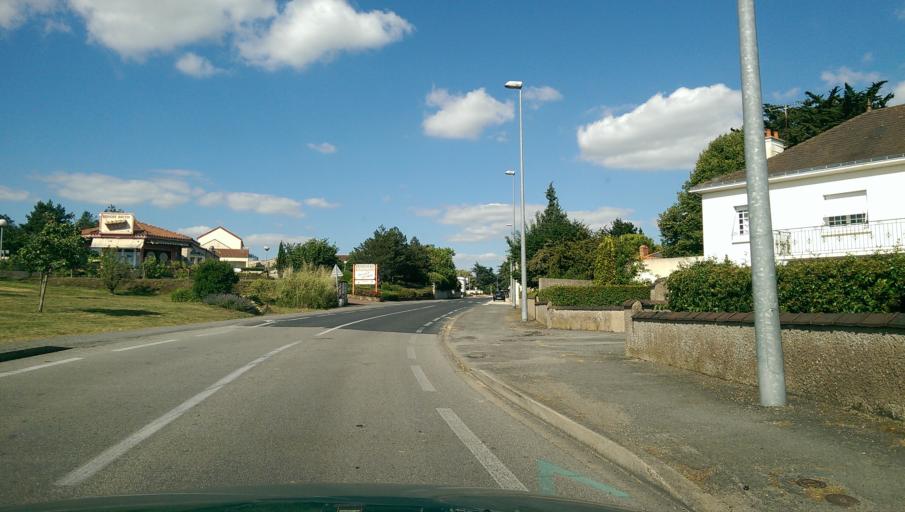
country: FR
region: Pays de la Loire
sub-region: Departement de la Vendee
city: Rocheserviere
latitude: 46.9389
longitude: -1.5136
